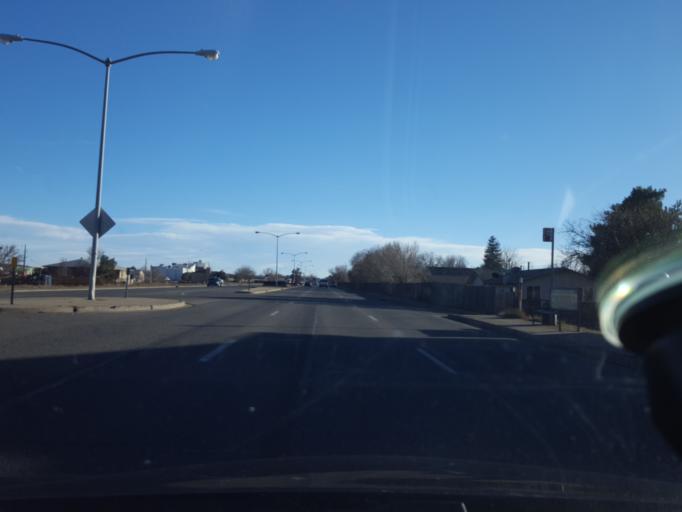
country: US
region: Colorado
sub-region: Adams County
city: Aurora
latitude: 39.7366
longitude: -104.7913
